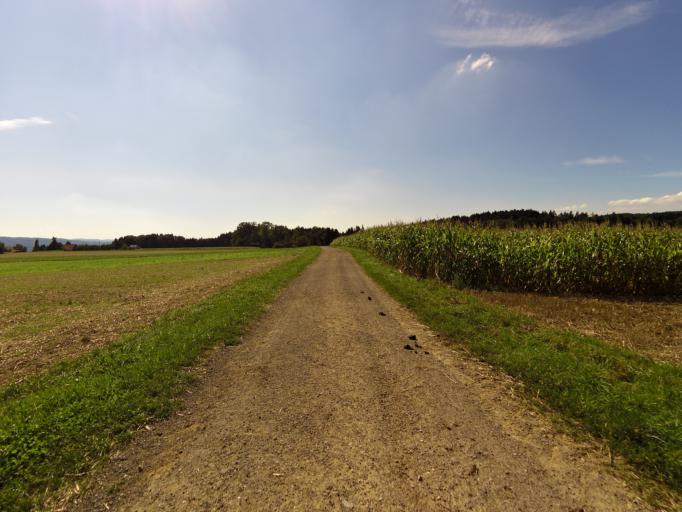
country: CH
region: Thurgau
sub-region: Weinfelden District
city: Wigoltingen
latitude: 47.6273
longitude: 9.0430
